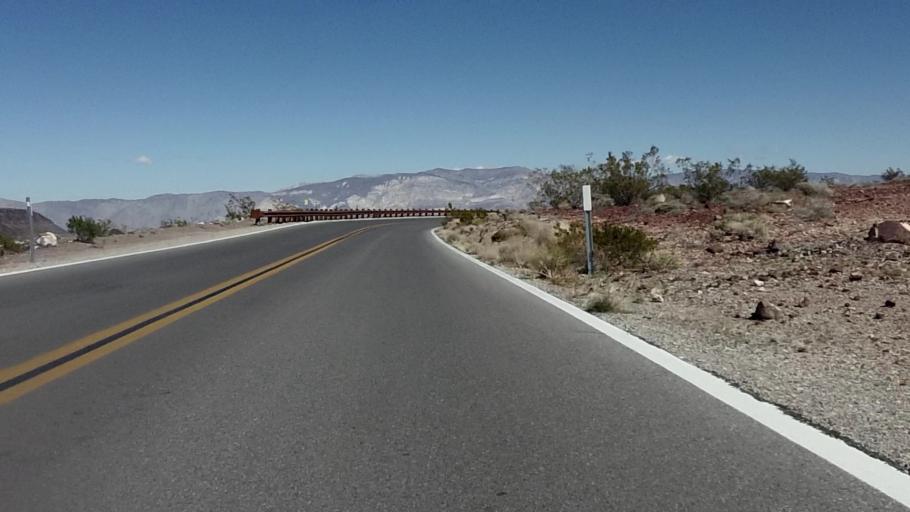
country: US
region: California
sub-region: Inyo County
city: Lone Pine
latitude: 36.3519
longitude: -117.5545
